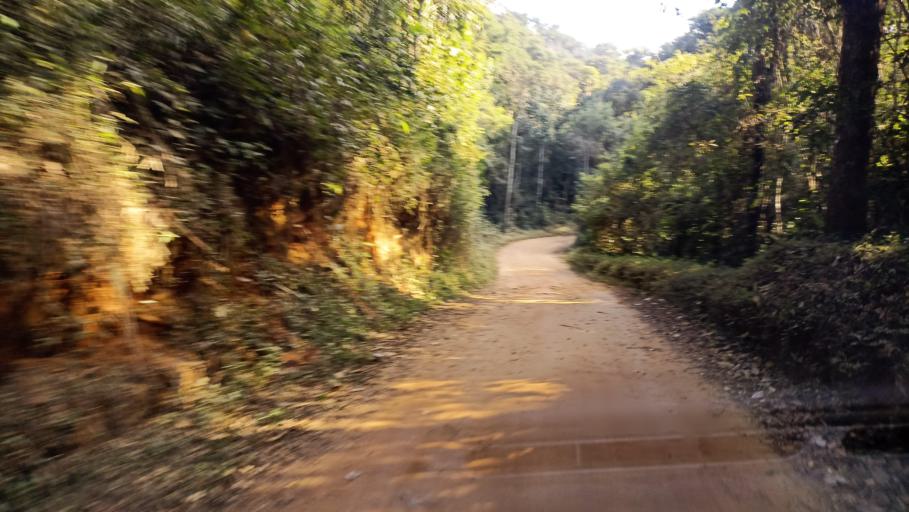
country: BR
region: Minas Gerais
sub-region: Ouro Preto
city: Ouro Preto
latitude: -20.3018
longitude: -43.5749
